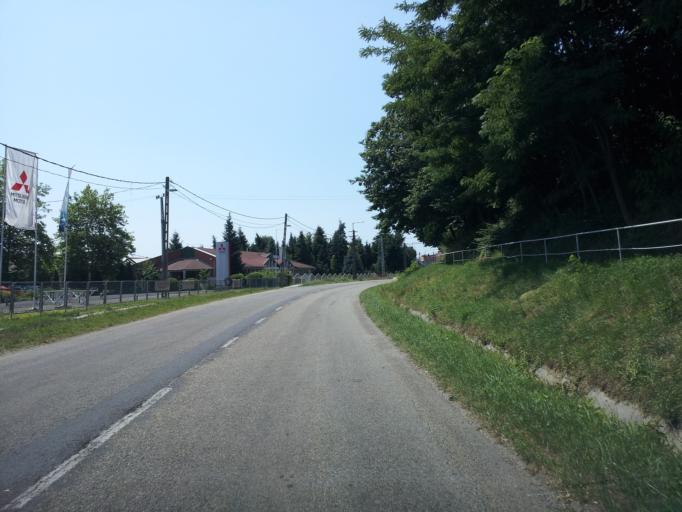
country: HU
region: Zala
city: Zalaegerszeg
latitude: 46.8575
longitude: 16.8501
